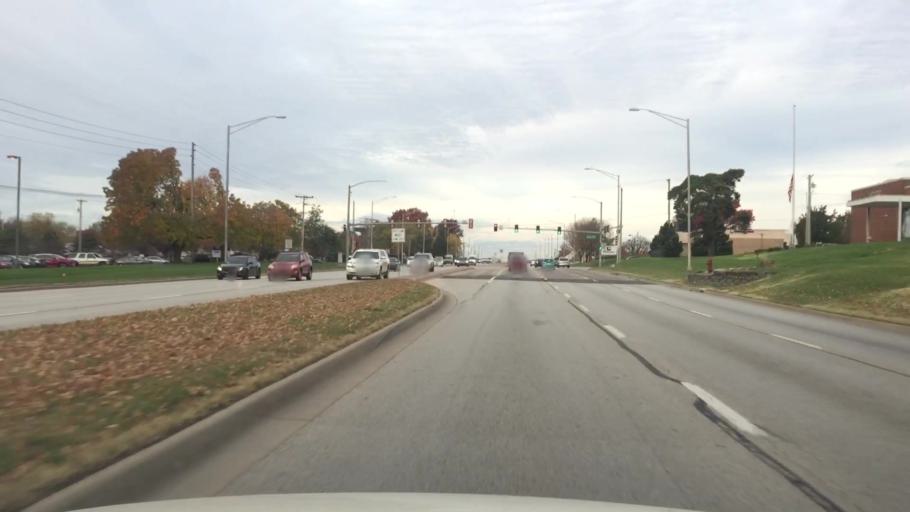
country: US
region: Kansas
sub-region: Johnson County
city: Shawnee
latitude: 39.0148
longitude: -94.7293
